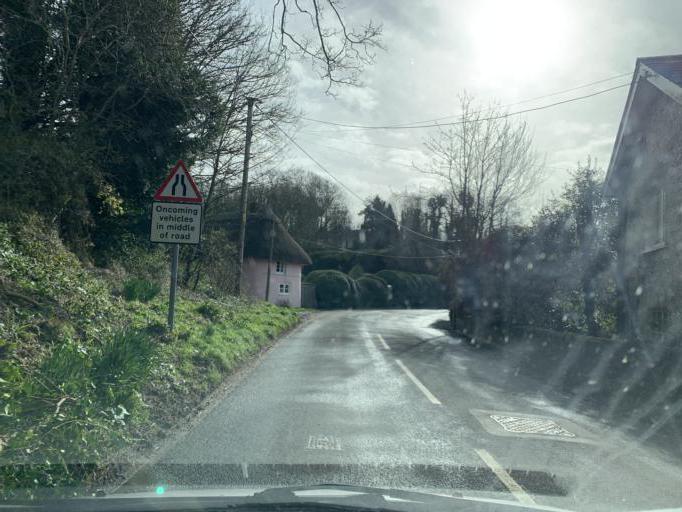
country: GB
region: England
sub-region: Wiltshire
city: Stapleford
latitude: 51.1336
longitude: -1.8984
